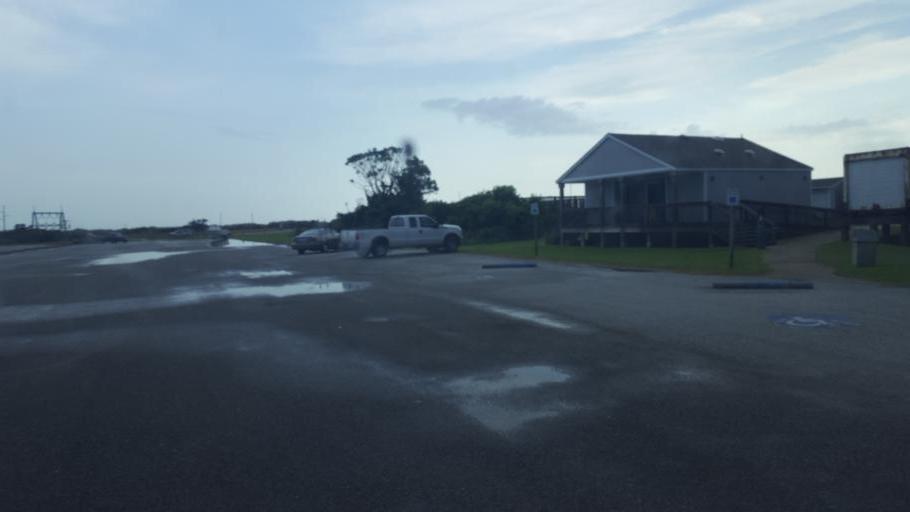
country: US
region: North Carolina
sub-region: Dare County
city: Wanchese
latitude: 35.7970
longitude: -75.5485
